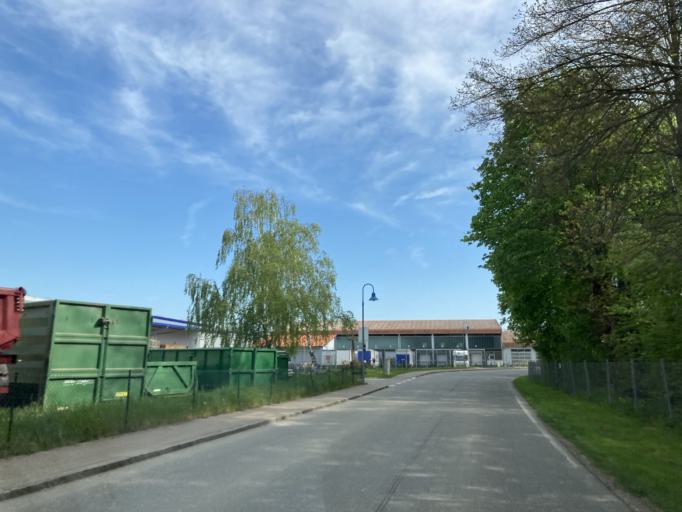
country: DE
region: Baden-Wuerttemberg
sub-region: Freiburg Region
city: Hartheim
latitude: 47.9381
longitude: 7.6506
